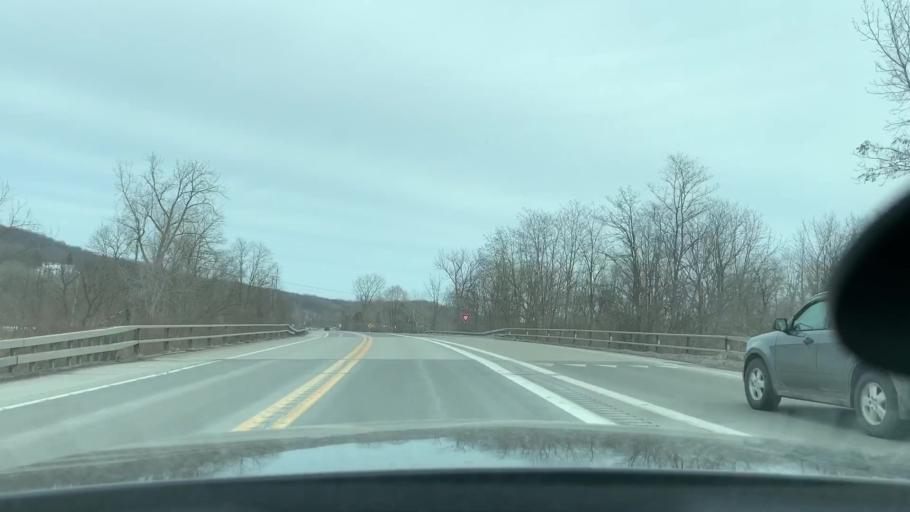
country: US
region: New York
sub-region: Herkimer County
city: Ilion
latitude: 43.0219
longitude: -75.0442
